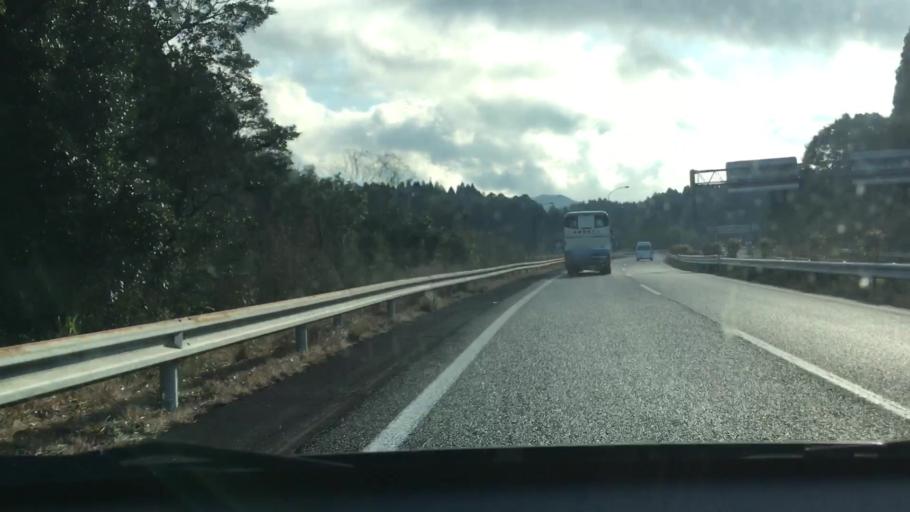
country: JP
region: Kagoshima
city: Okuchi-shinohara
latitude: 32.0297
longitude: 130.7973
